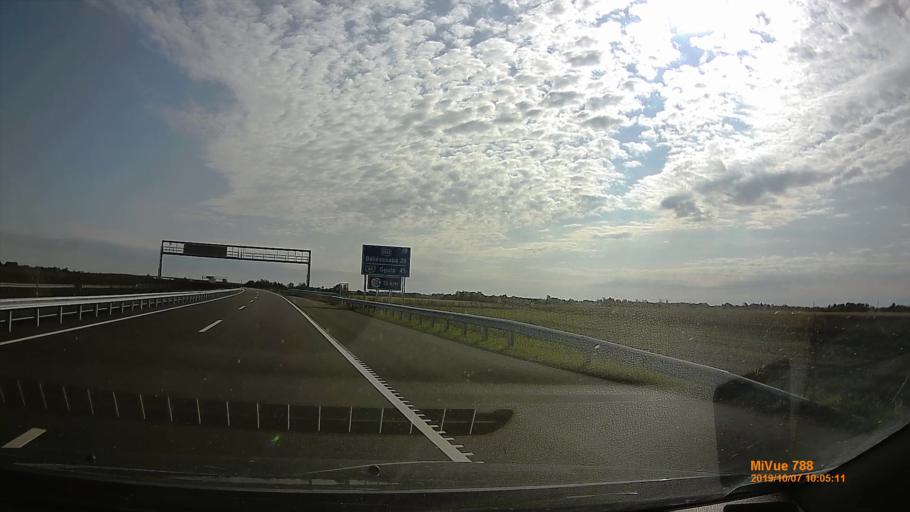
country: HU
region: Bekes
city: Kondoros
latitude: 46.7376
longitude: 20.7930
